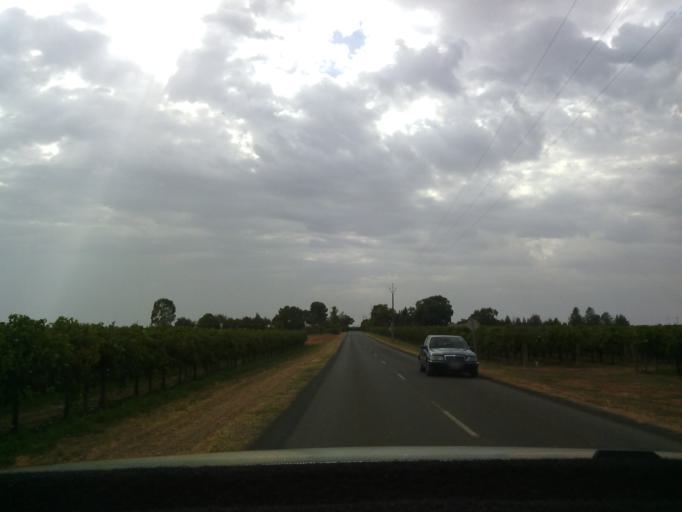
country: AU
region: South Australia
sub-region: Berri and Barmera
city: Monash
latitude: -34.2633
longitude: 140.5712
